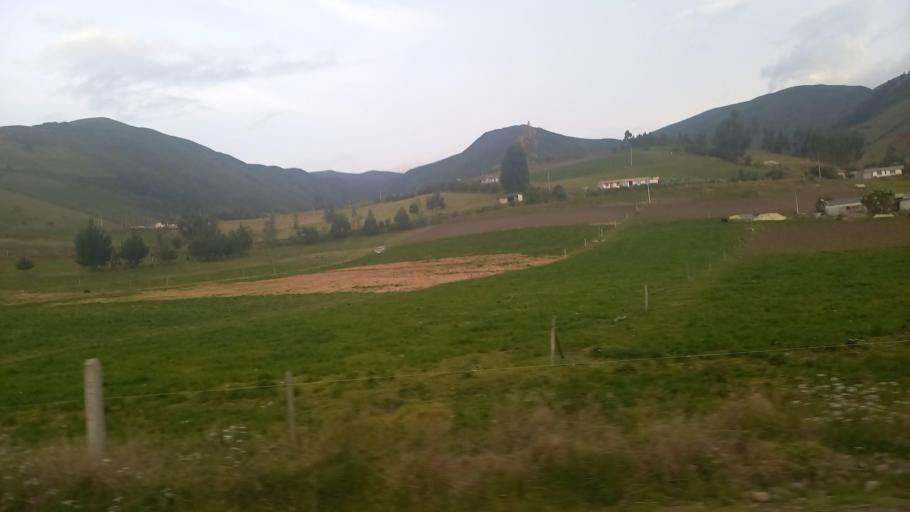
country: EC
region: Pichincha
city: Cayambe
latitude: 0.1108
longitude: -78.0786
